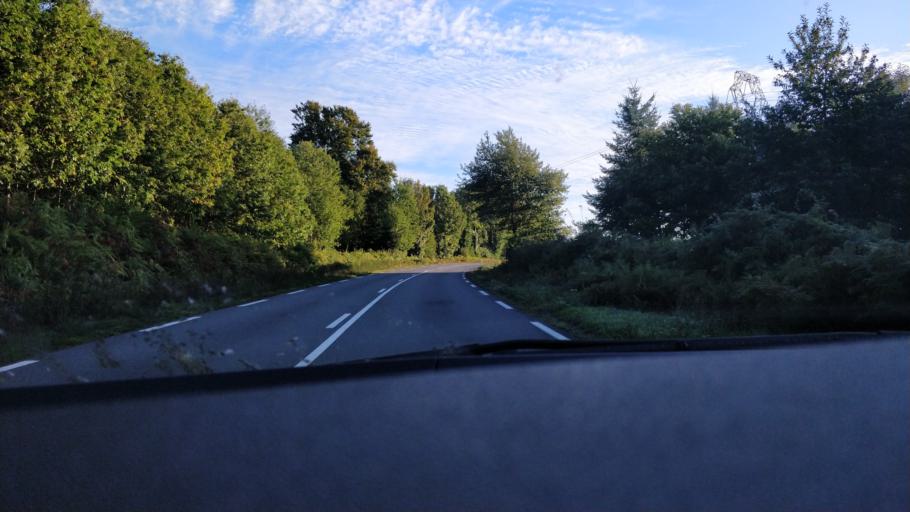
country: FR
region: Limousin
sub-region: Departement de la Haute-Vienne
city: Sauviat-sur-Vige
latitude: 45.9415
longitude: 1.6659
